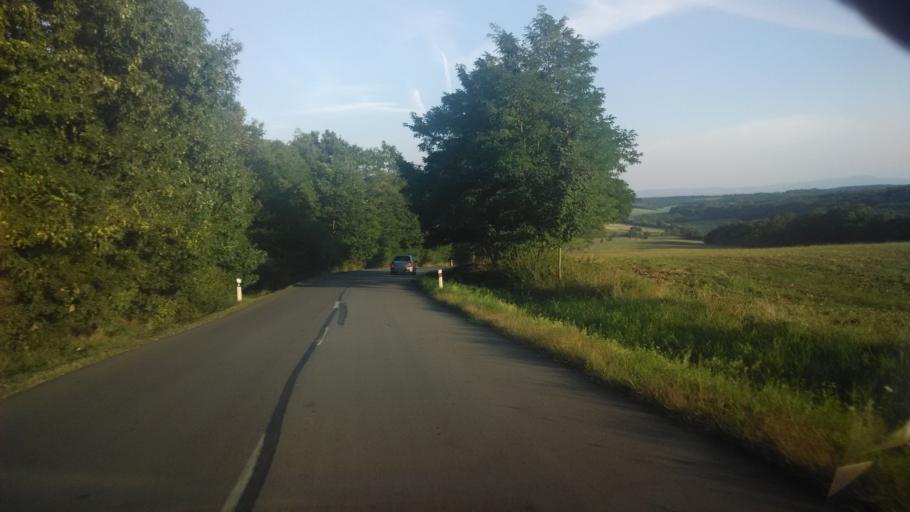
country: SK
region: Banskobystricky
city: Dudince
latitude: 48.2168
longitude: 18.7804
